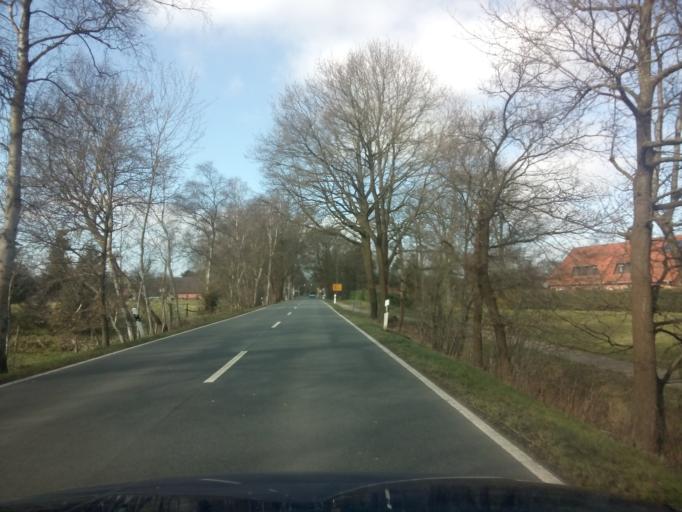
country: DE
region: Lower Saxony
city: Worpswede
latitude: 53.2148
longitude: 8.9529
